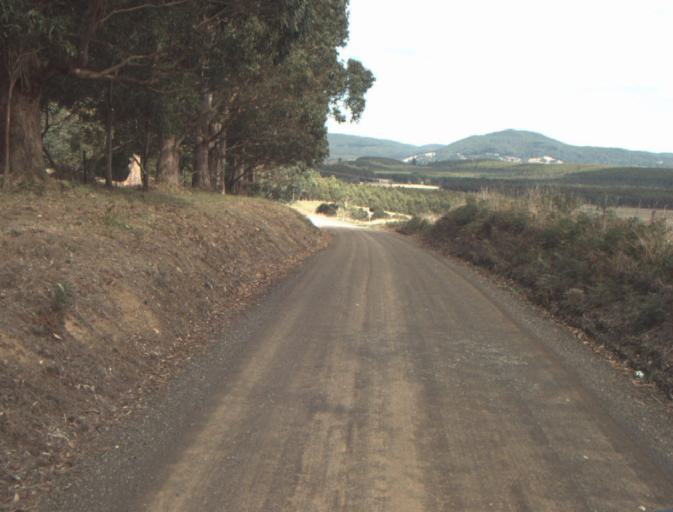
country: AU
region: Tasmania
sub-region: Launceston
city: Mayfield
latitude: -41.1912
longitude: 147.1800
